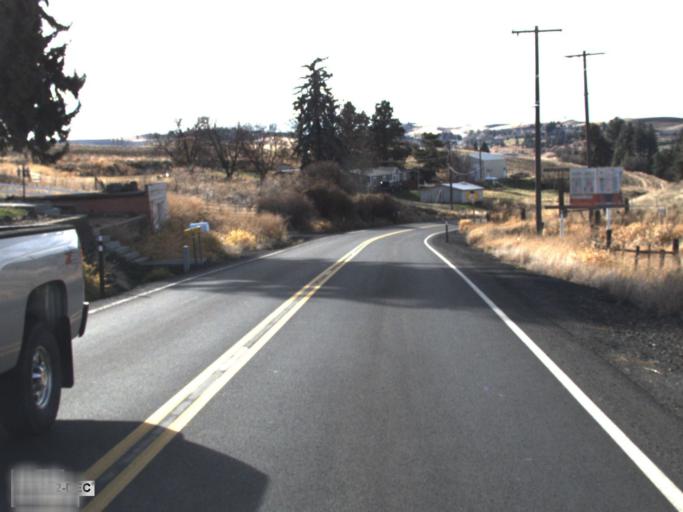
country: US
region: Washington
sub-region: Whitman County
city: Colfax
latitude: 46.8835
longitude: -117.3527
